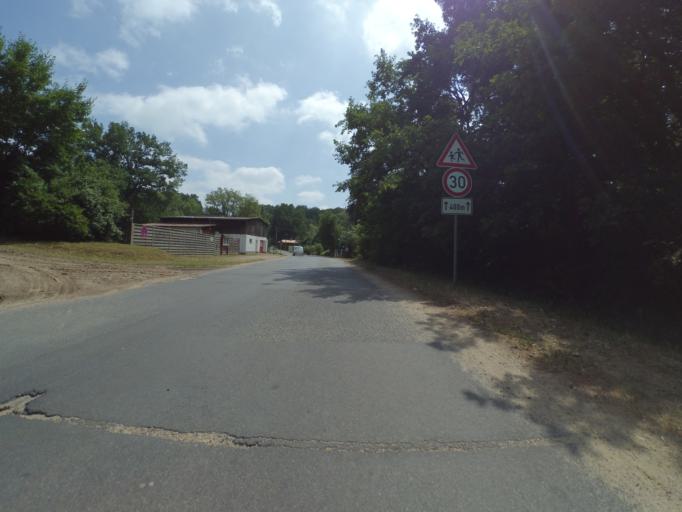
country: DE
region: Mecklenburg-Vorpommern
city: Plau am See
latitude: 53.4318
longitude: 12.3195
